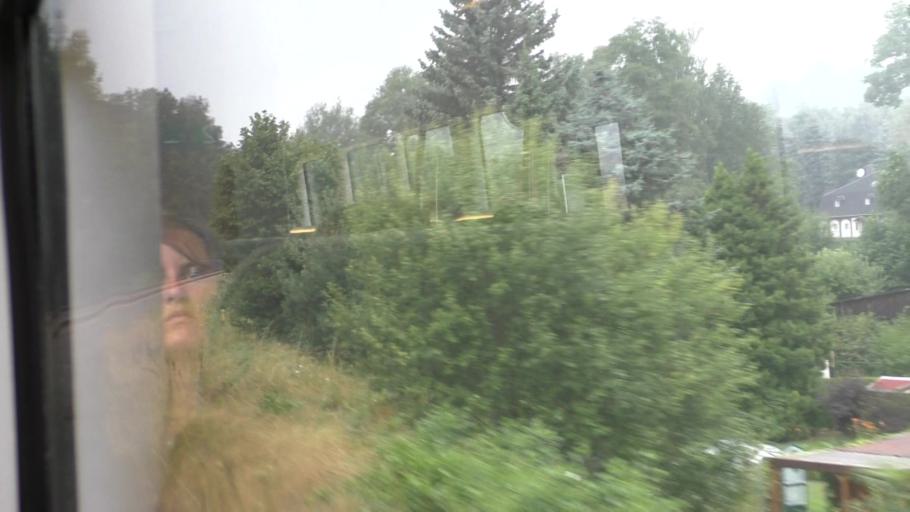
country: DE
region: Saxony
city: Neugersdorf
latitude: 50.9864
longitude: 14.6036
